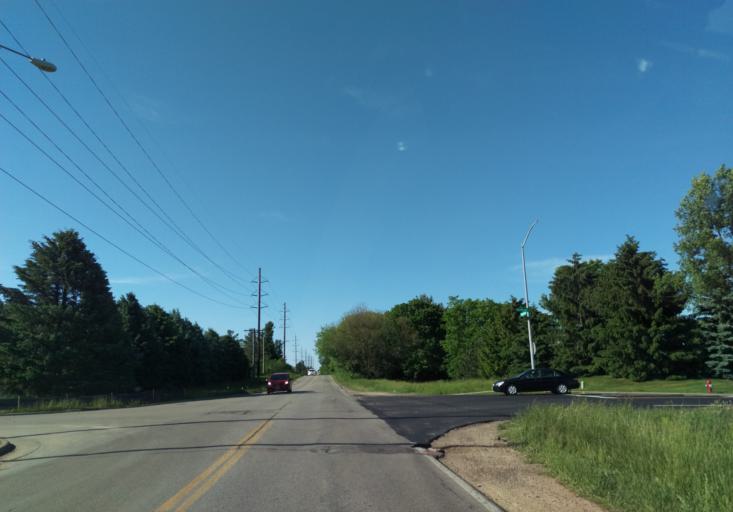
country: US
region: Wisconsin
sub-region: Dane County
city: Middleton
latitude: 43.0818
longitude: -89.5368
